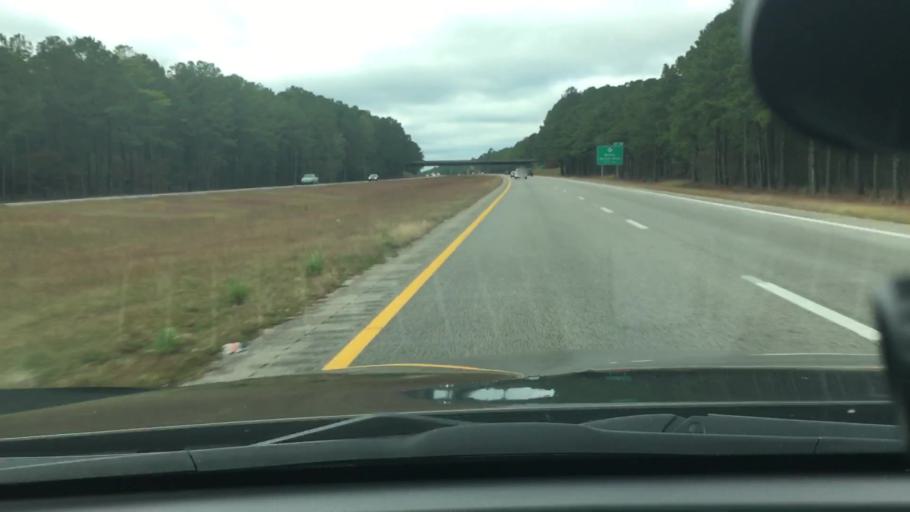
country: US
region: North Carolina
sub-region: Nash County
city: Spring Hope
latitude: 35.7845
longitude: -78.0938
